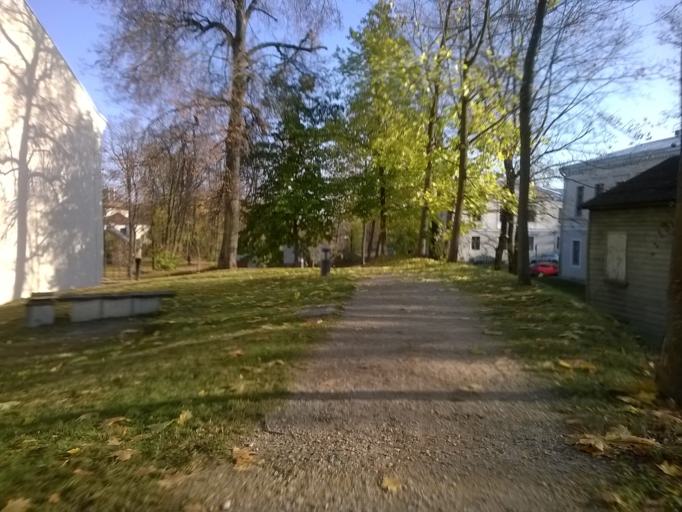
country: EE
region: Tartu
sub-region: Tartu linn
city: Tartu
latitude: 58.3788
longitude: 26.7166
